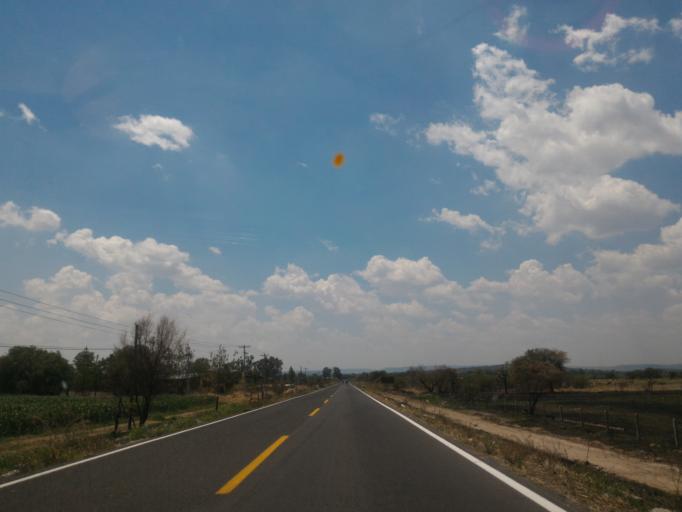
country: MX
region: Guanajuato
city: Ciudad Manuel Doblado
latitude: 20.7784
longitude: -101.9774
